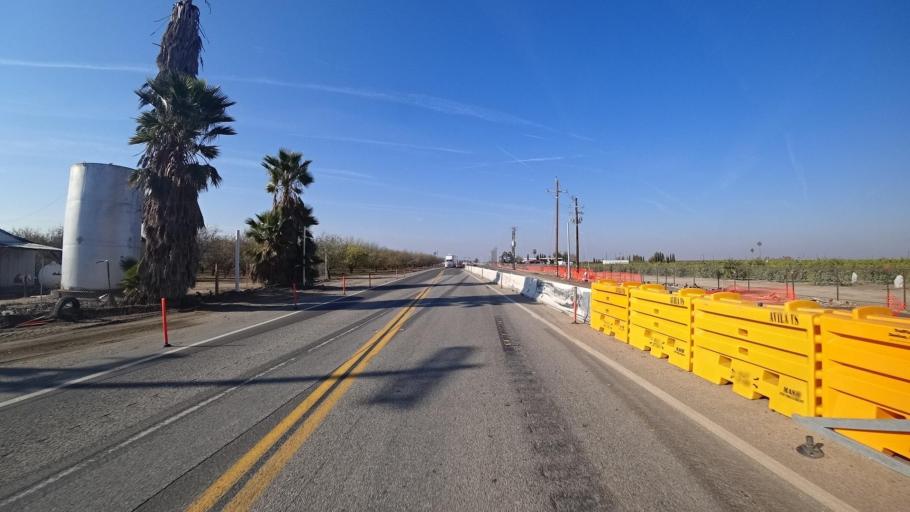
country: US
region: California
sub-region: Kern County
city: Weedpatch
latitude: 35.2087
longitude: -118.9100
